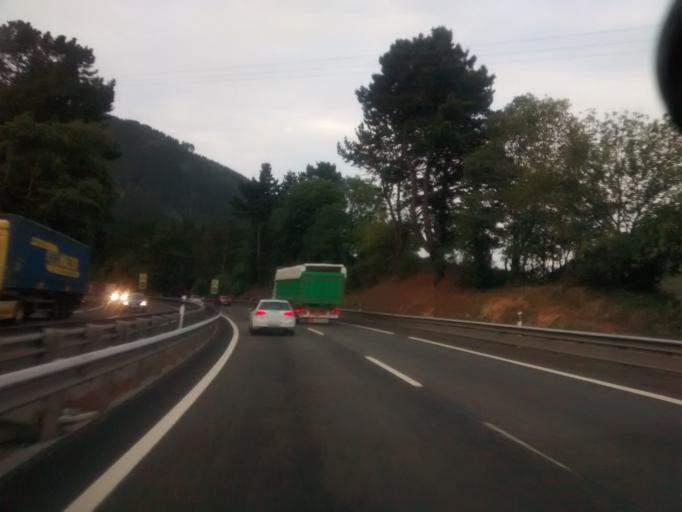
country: ES
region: Basque Country
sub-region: Provincia de Guipuzcoa
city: Elgoibar
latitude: 43.2118
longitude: -2.4157
